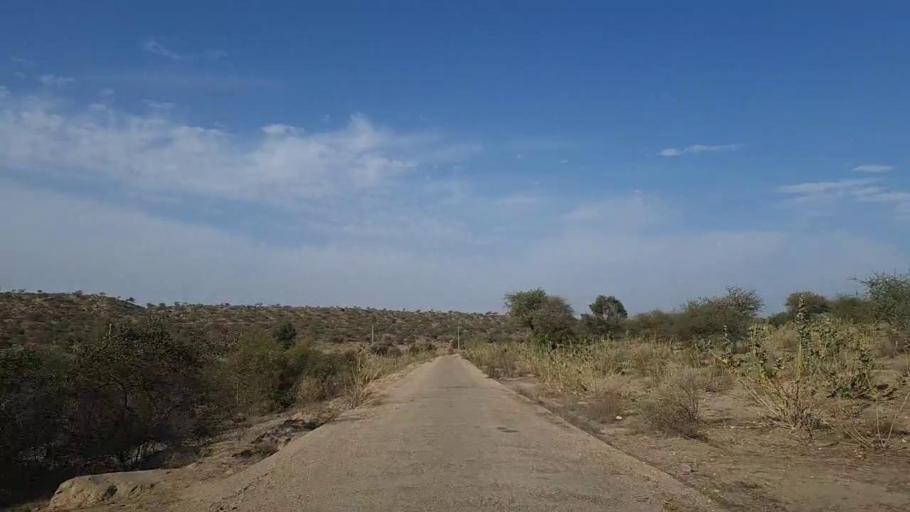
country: PK
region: Sindh
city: Naukot
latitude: 24.8473
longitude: 69.5172
